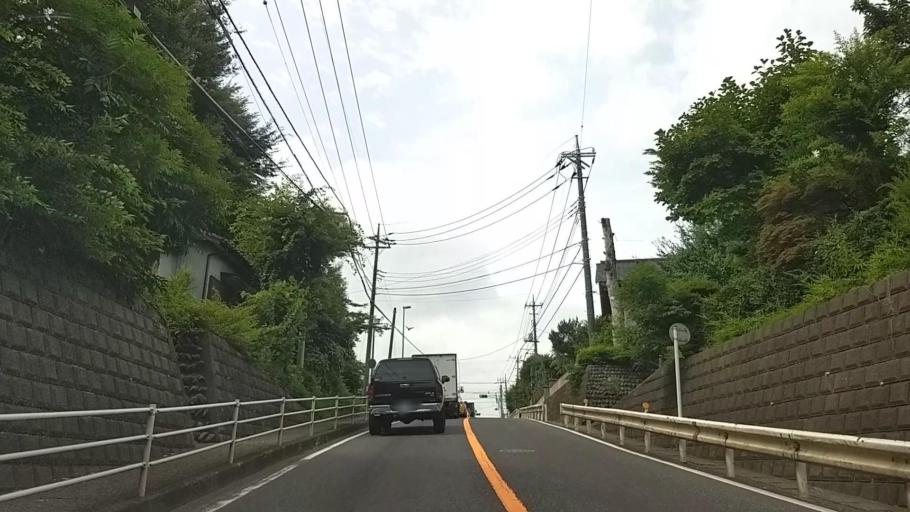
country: JP
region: Kanagawa
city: Minami-rinkan
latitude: 35.4537
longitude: 139.4744
